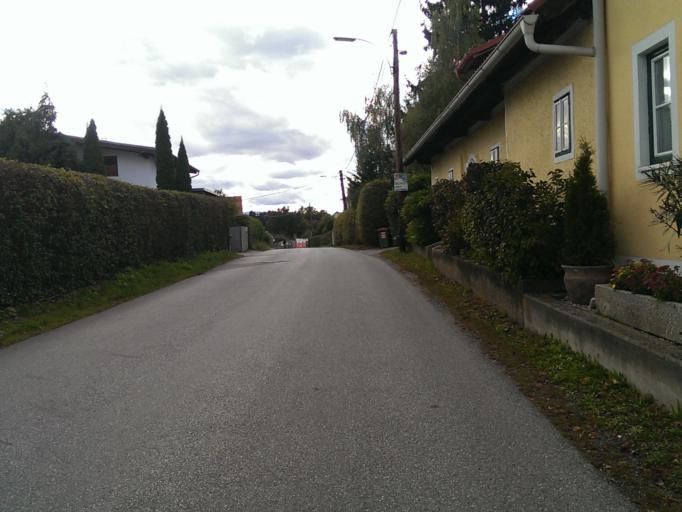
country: AT
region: Styria
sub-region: Politischer Bezirk Graz-Umgebung
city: Raaba
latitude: 47.0546
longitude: 15.4951
